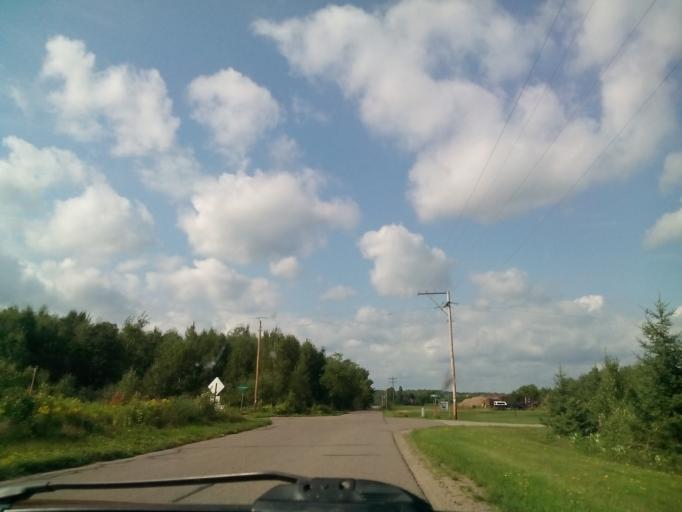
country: US
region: Wisconsin
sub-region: Menominee County
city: Legend Lake
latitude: 45.3082
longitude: -88.5221
